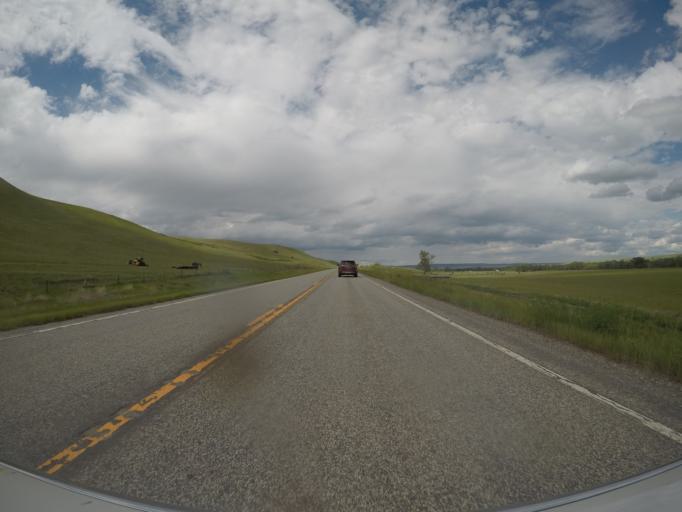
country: US
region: Montana
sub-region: Sweet Grass County
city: Big Timber
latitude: 45.7987
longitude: -109.9698
